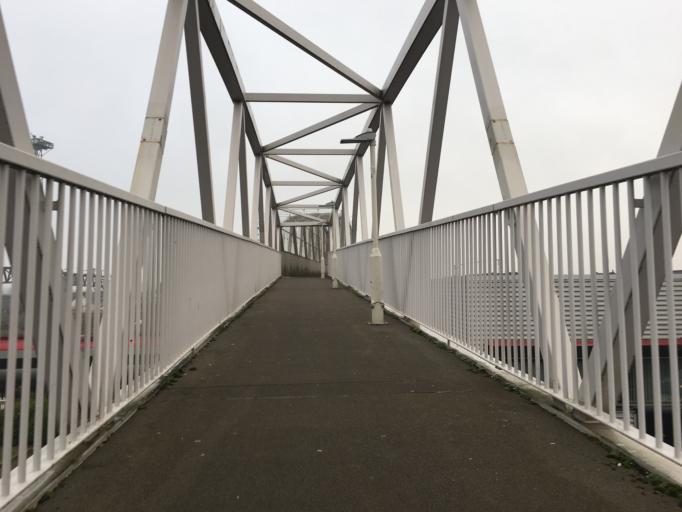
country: GB
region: England
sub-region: Warwickshire
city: Rugby
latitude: 52.3799
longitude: -1.2583
